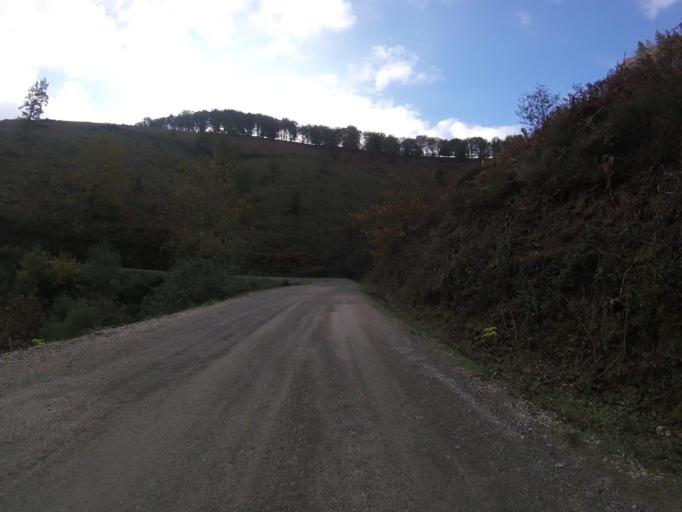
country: ES
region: Navarre
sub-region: Provincia de Navarra
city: Goizueta
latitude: 43.2120
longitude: -1.8409
